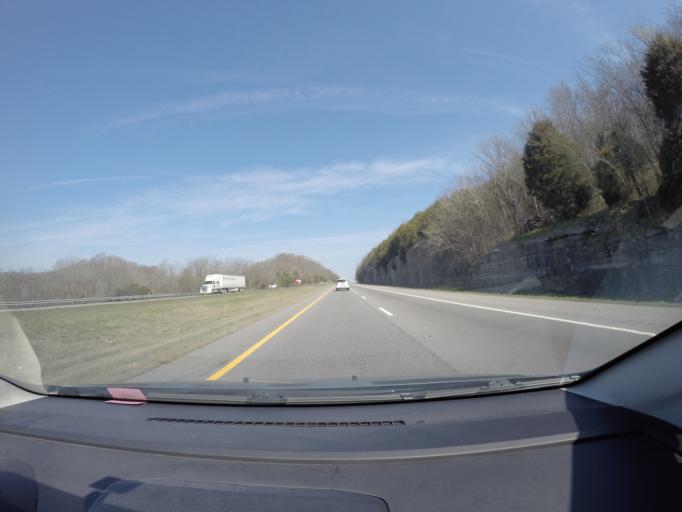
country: US
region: Tennessee
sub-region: Rutherford County
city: Plainview
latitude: 35.5855
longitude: -86.2360
